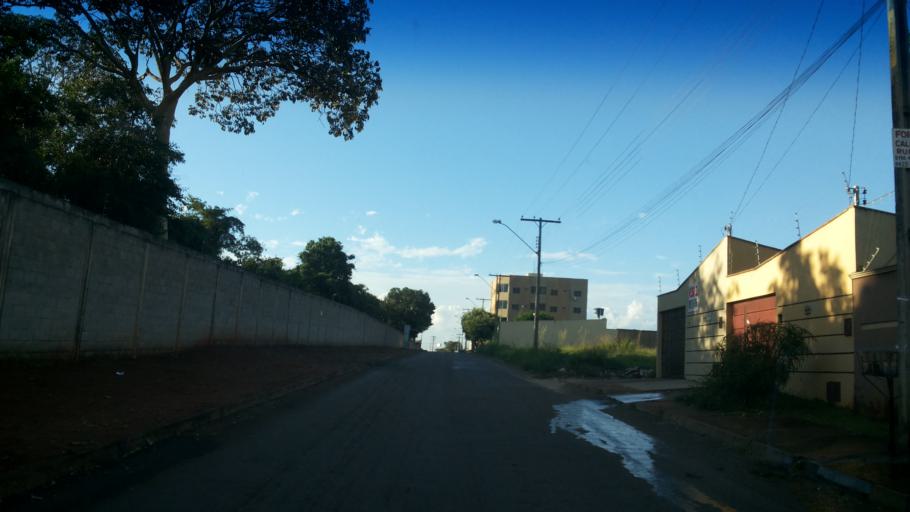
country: BR
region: Goias
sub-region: Goiania
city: Goiania
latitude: -16.6455
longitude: -49.3016
